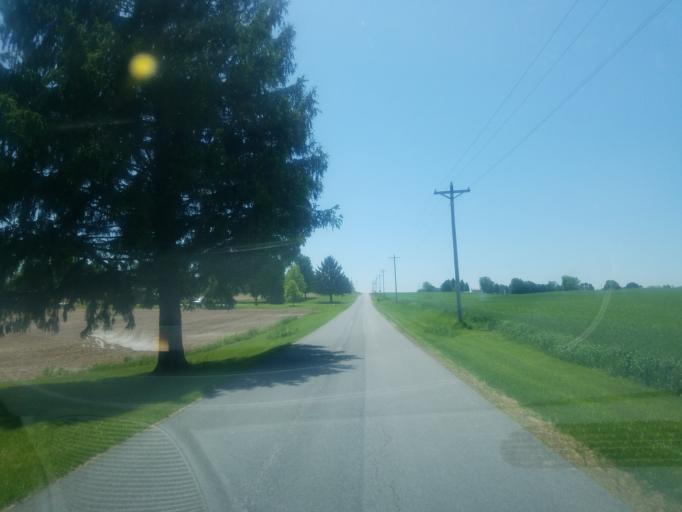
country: US
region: Ohio
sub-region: Huron County
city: New London
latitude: 41.0952
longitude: -82.4624
